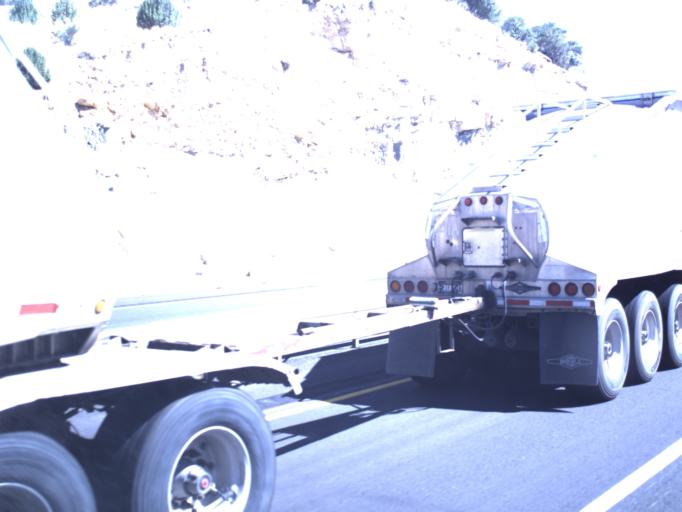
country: US
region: Utah
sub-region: Sevier County
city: Salina
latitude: 38.9159
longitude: -111.7256
